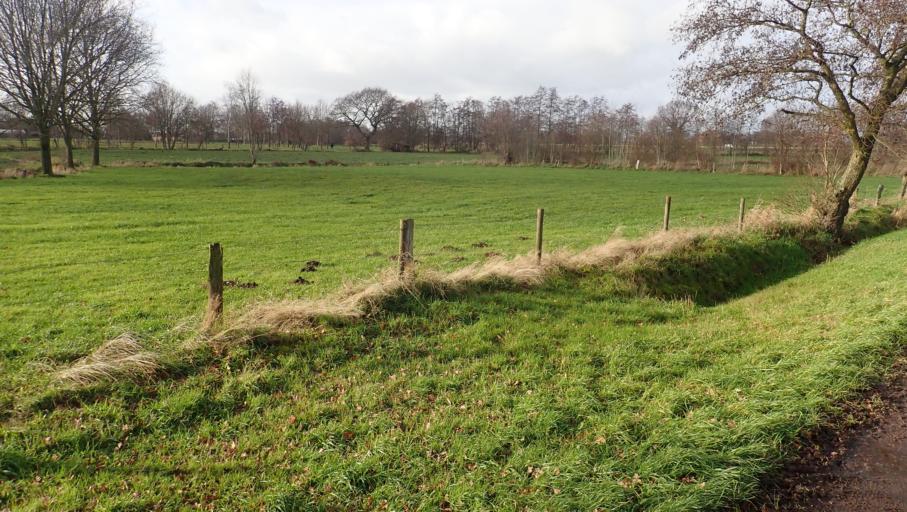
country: BE
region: Flanders
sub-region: Provincie Antwerpen
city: Brecht
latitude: 51.3690
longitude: 4.6583
